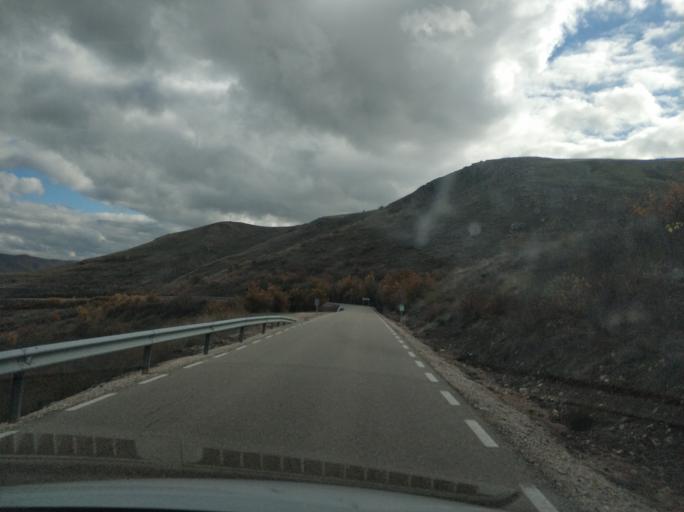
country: ES
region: Castille and Leon
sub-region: Provincia de Soria
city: Medinaceli
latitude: 41.1648
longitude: -2.4330
